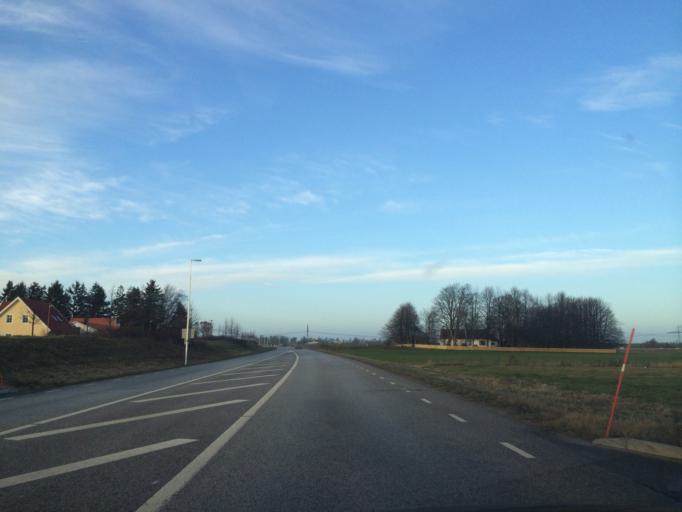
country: SE
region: Skane
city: Bjarred
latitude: 55.7344
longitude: 13.0407
